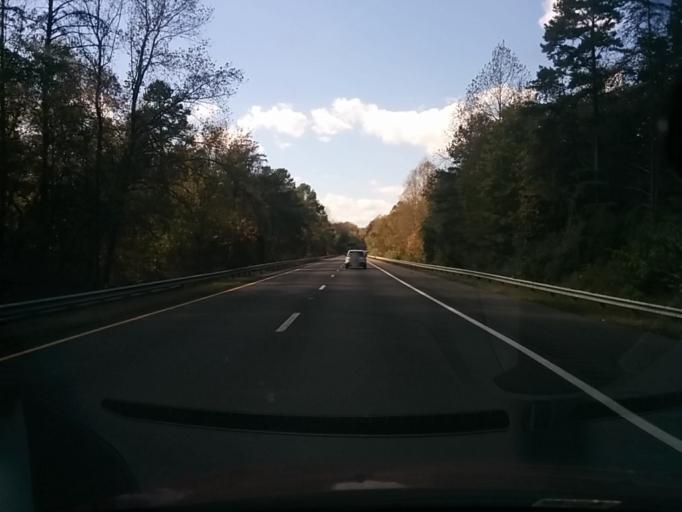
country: US
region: Virginia
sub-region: Albemarle County
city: Crozet
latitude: 38.0316
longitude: -78.6750
